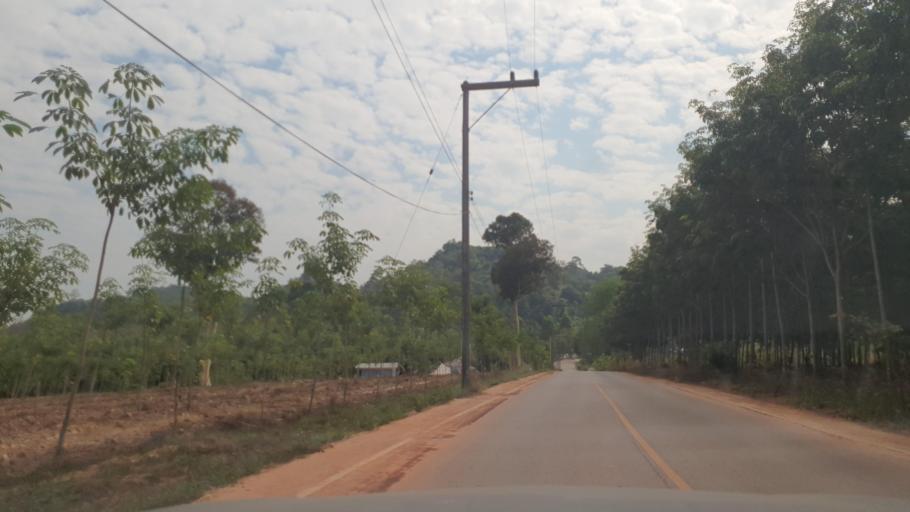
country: TH
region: Changwat Bueng Kan
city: Si Wilai
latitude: 18.2778
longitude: 103.7949
